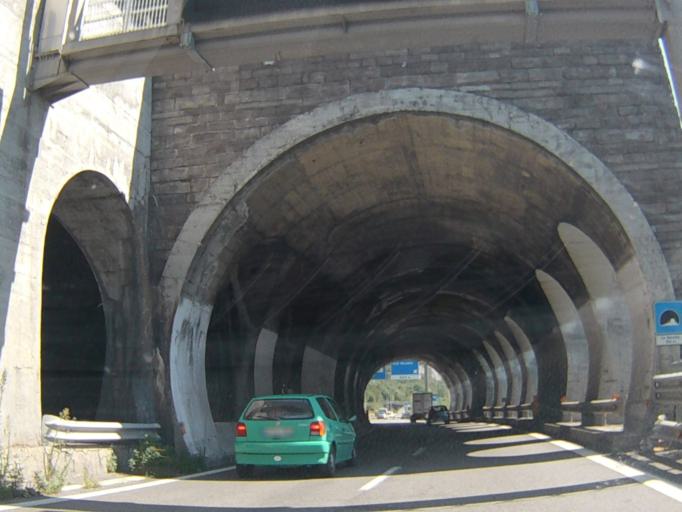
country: IT
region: Lombardy
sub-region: Provincia di Lecco
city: Abbadia Lariana
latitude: 45.8836
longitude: 9.3632
